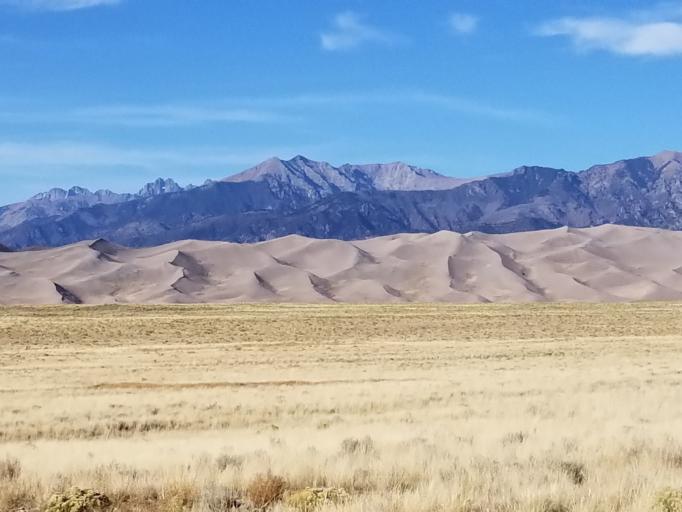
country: US
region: Colorado
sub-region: Alamosa County
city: Alamosa East
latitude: 37.7040
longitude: -105.5377
